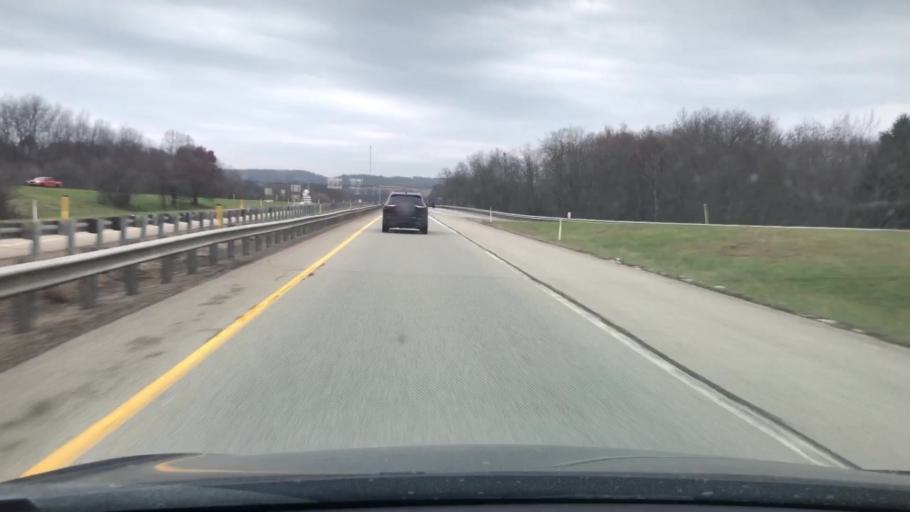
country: US
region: Pennsylvania
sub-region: Armstrong County
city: West Hills
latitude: 40.8098
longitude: -79.5550
